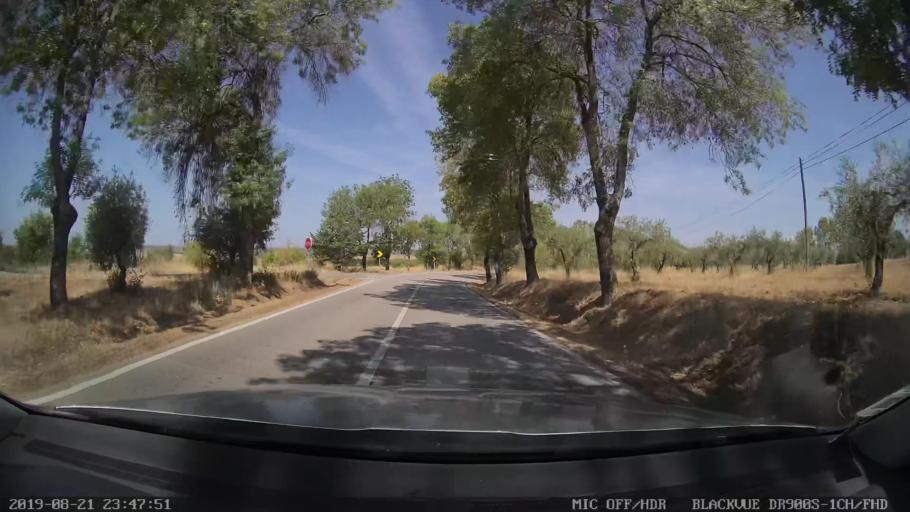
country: PT
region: Castelo Branco
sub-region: Idanha-A-Nova
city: Idanha-a-Nova
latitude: 39.8570
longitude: -7.2592
